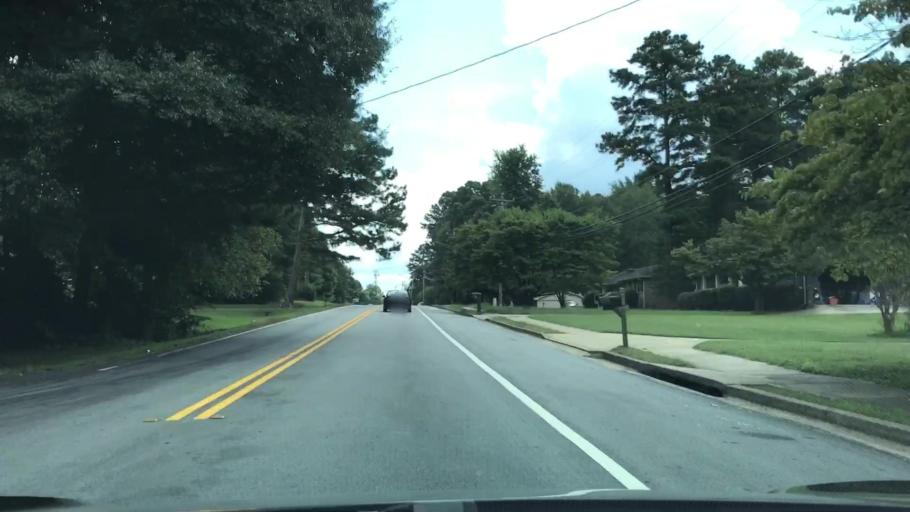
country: US
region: Georgia
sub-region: Gwinnett County
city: Snellville
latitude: 33.8914
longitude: -84.0664
